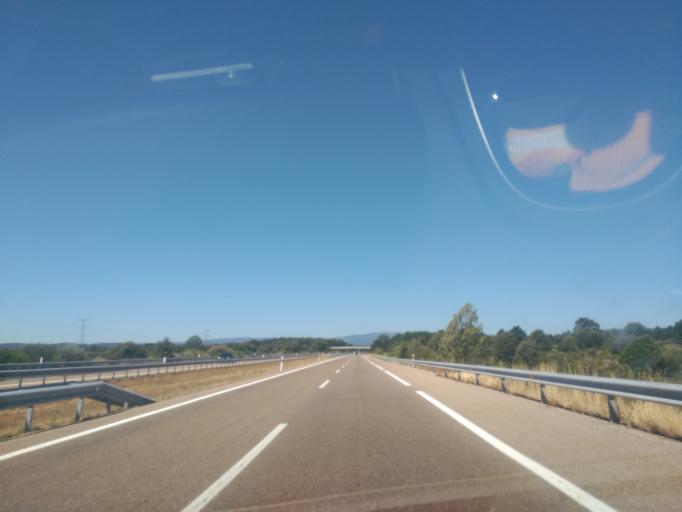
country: ES
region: Castille and Leon
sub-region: Provincia de Zamora
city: Asturianos
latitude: 42.0434
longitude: -6.4762
